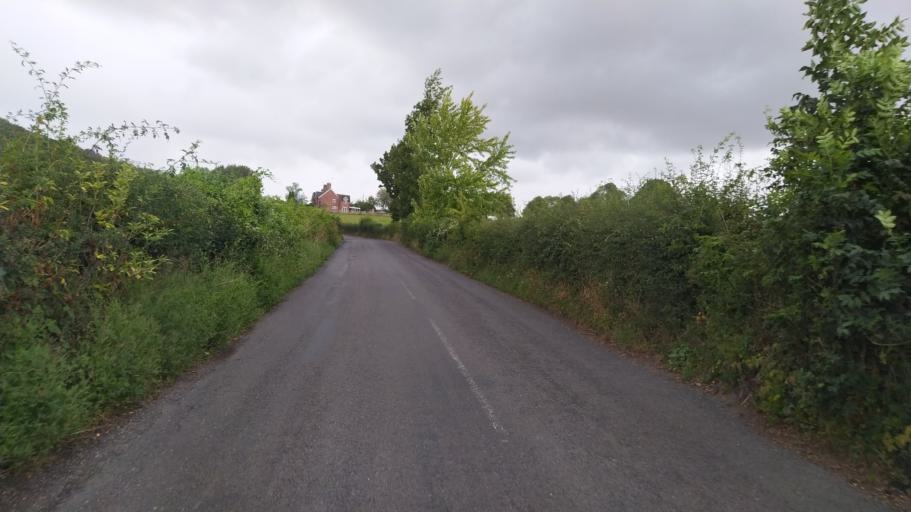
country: GB
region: England
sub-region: Hampshire
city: Four Marks
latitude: 51.0078
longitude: -1.0487
